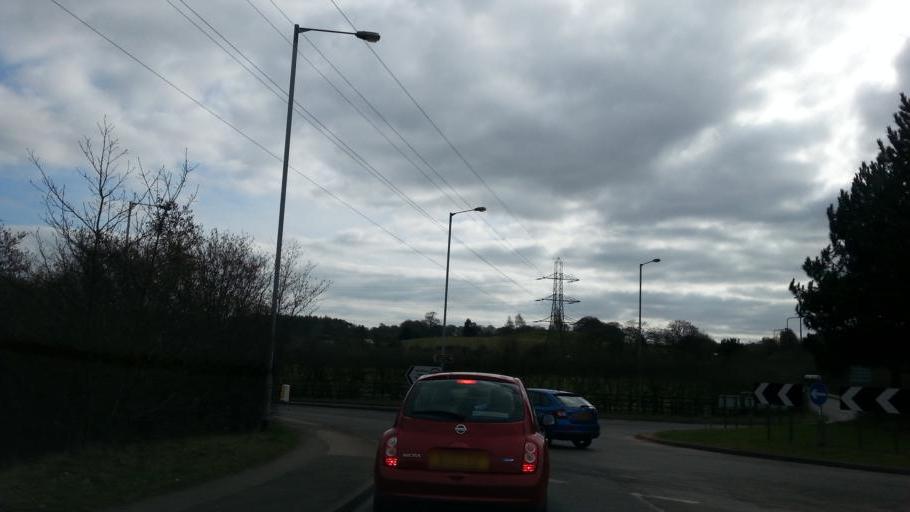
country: GB
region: England
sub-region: Staffordshire
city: Rugeley
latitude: 52.7469
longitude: -1.9119
